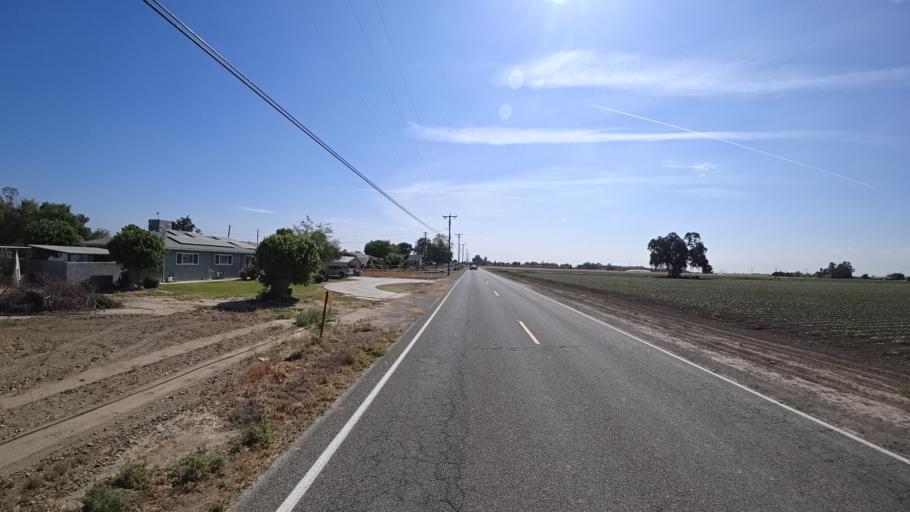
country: US
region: California
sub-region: Kings County
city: Lemoore
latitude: 36.2546
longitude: -119.7668
